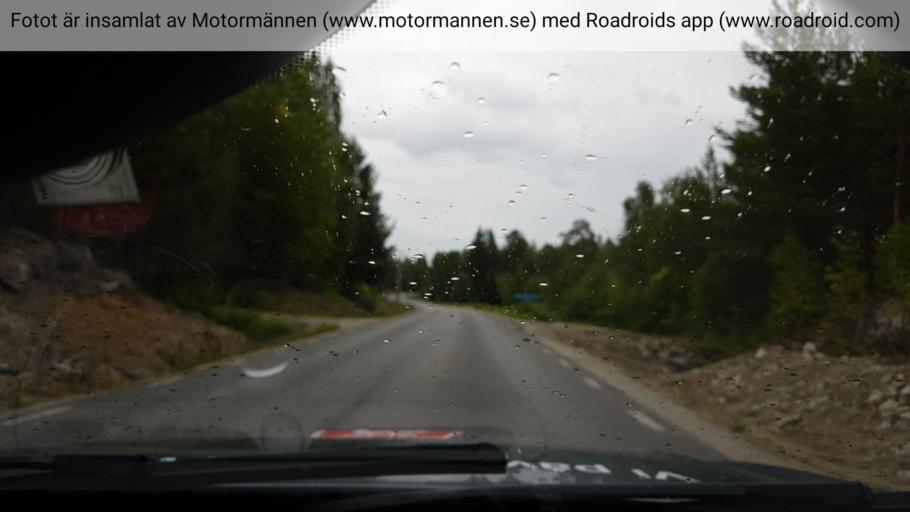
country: SE
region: Jaemtland
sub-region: Braecke Kommun
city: Braecke
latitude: 62.3905
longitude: 15.0706
